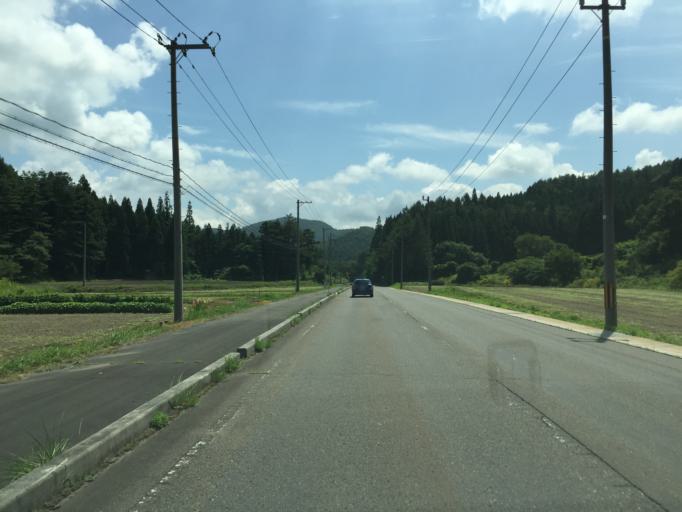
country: JP
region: Fukushima
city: Inawashiro
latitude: 37.4108
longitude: 140.0561
